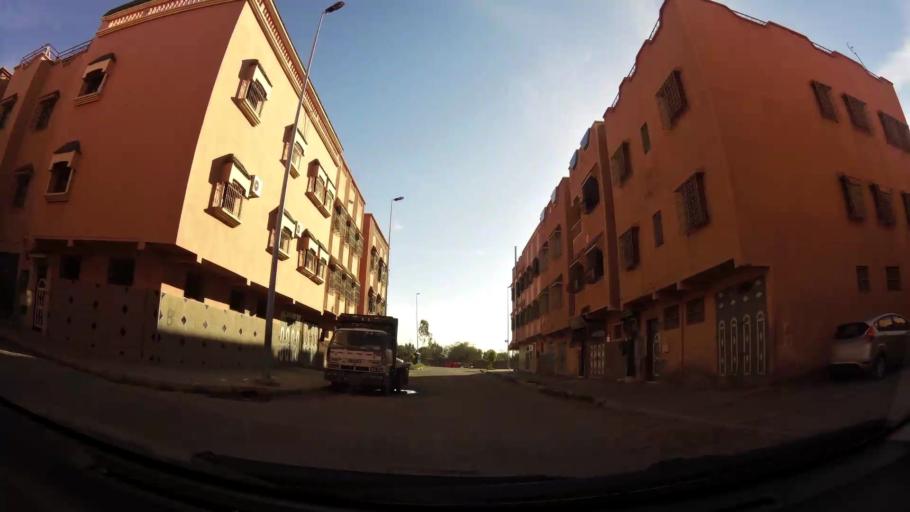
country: MA
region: Marrakech-Tensift-Al Haouz
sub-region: Marrakech
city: Marrakesh
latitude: 31.6198
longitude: -8.0700
